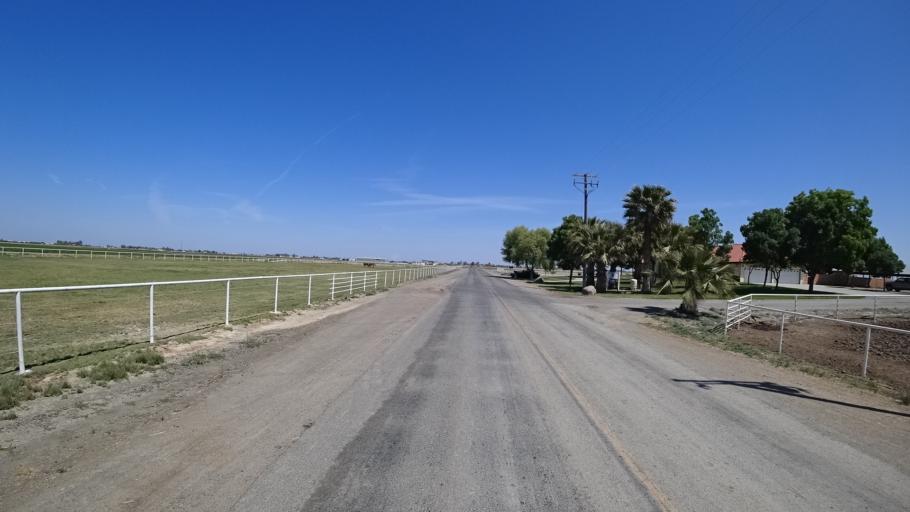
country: US
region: California
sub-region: Kings County
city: Stratford
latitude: 36.2096
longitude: -119.7623
